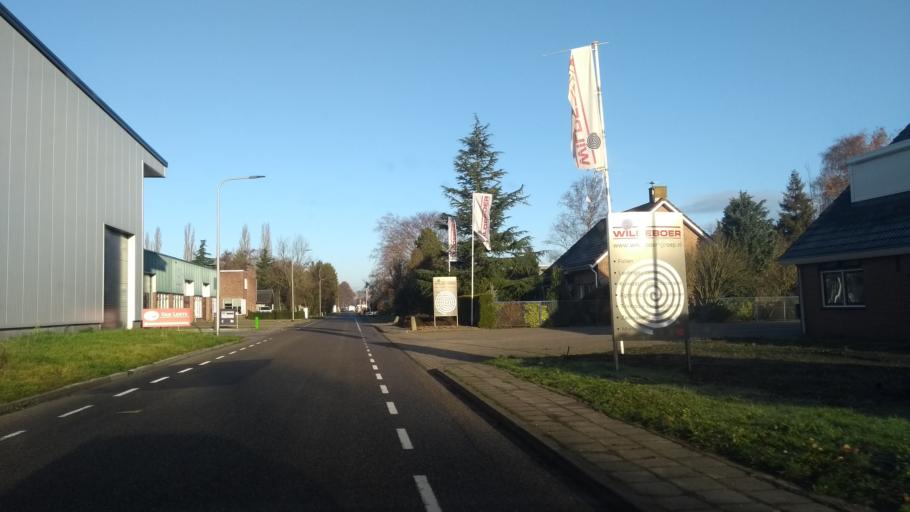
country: NL
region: Overijssel
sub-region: Gemeente Dalfsen
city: Dalfsen
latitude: 52.5941
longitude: 6.2854
